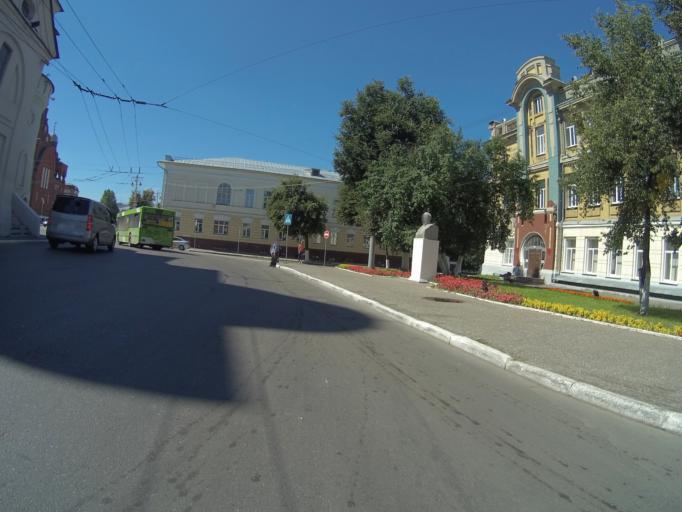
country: RU
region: Vladimir
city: Vladimir
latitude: 56.1271
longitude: 40.3973
